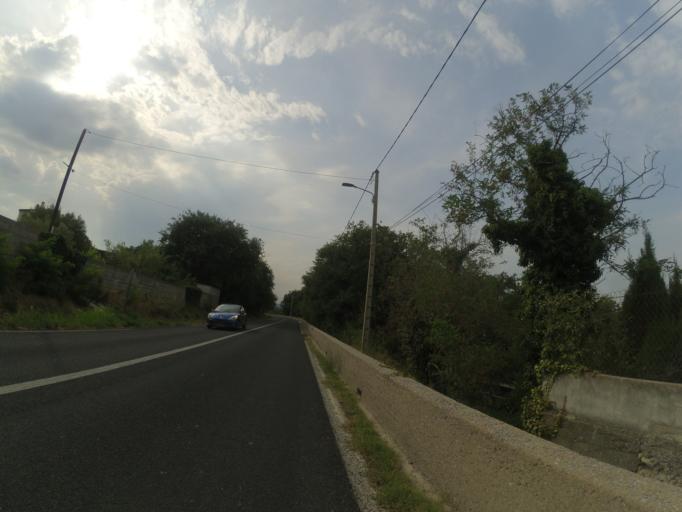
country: FR
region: Languedoc-Roussillon
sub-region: Departement des Pyrenees-Orientales
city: Corneilla-la-Riviere
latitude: 42.6809
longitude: 2.7472
